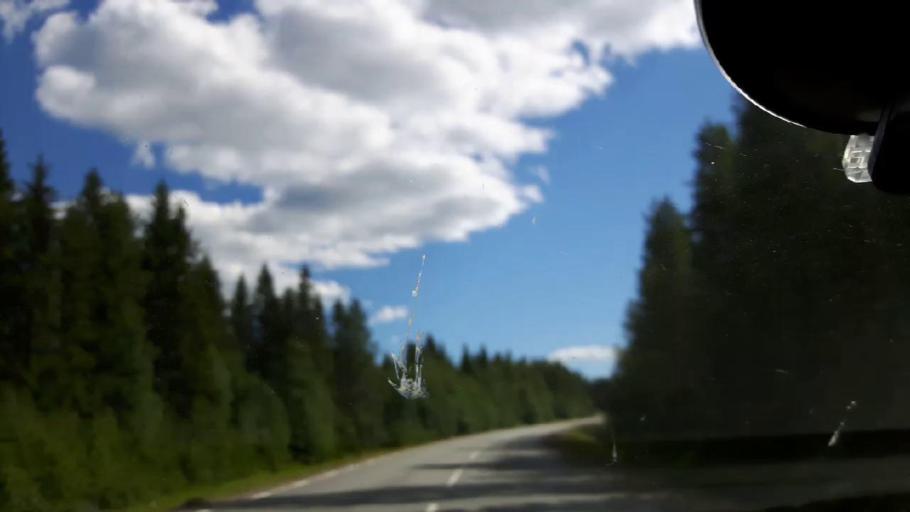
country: SE
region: Vaesternorrland
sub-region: Ange Kommun
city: Fransta
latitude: 62.8178
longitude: 16.2030
